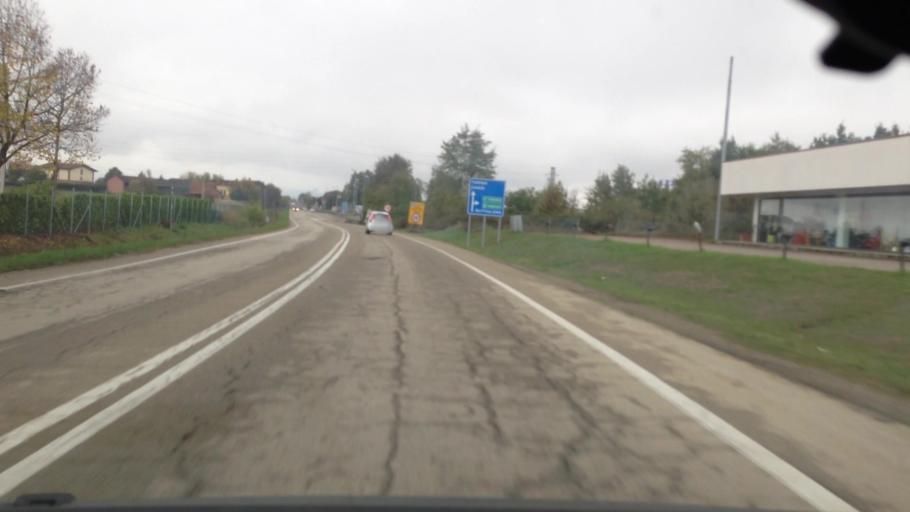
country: IT
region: Piedmont
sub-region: Provincia di Asti
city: Villanova d'Asti
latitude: 44.9582
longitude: 7.9134
